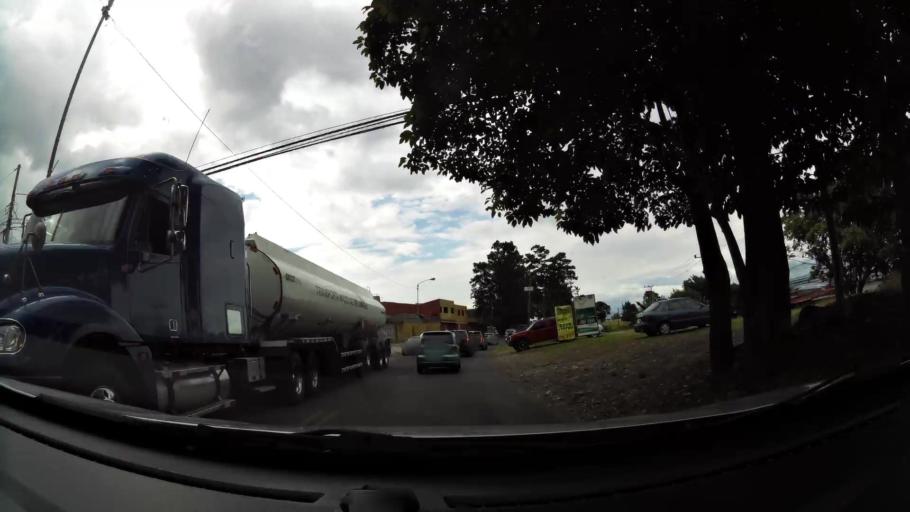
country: CR
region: San Jose
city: San Felipe
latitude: 9.9153
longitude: -84.1158
